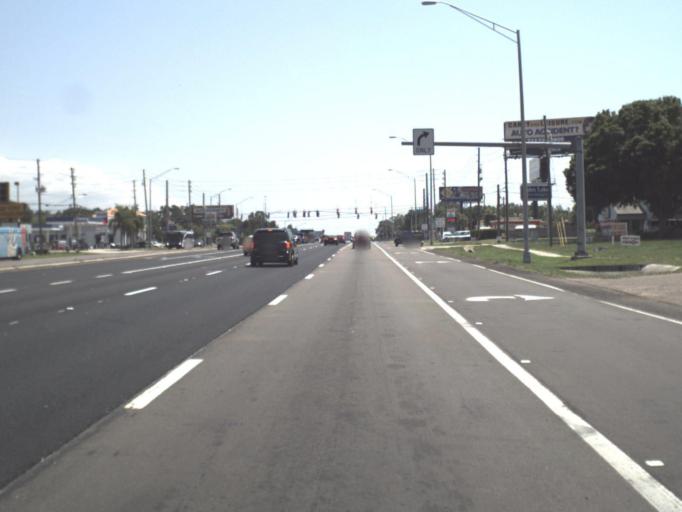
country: US
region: Florida
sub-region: Pinellas County
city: Saint George
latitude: 28.0692
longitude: -82.7390
